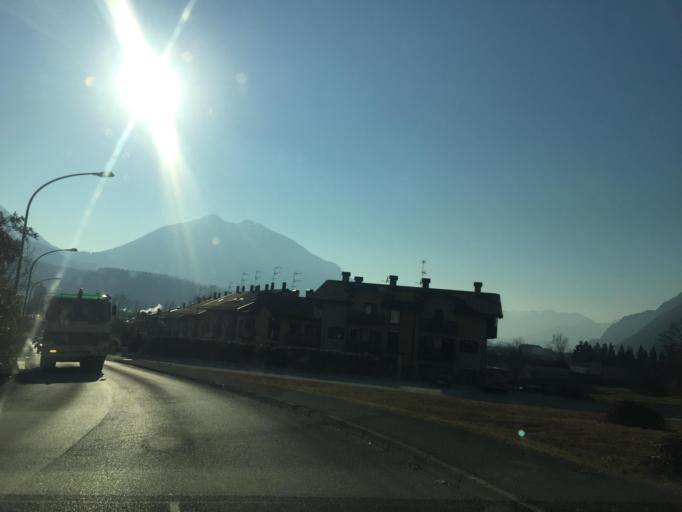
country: IT
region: Friuli Venezia Giulia
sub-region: Provincia di Udine
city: Tolmezzo
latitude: 46.3994
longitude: 13.0295
